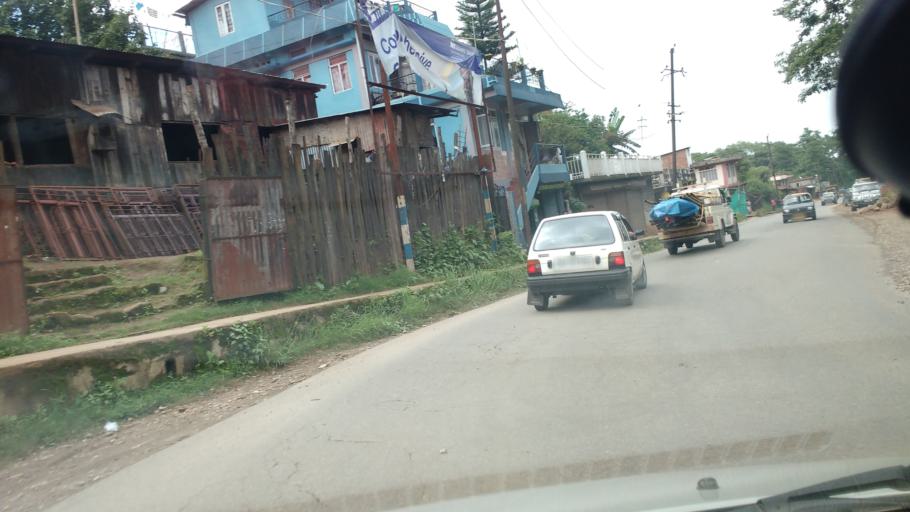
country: IN
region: Meghalaya
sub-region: East Khasi Hills
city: Shillong
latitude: 25.5636
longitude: 91.8542
